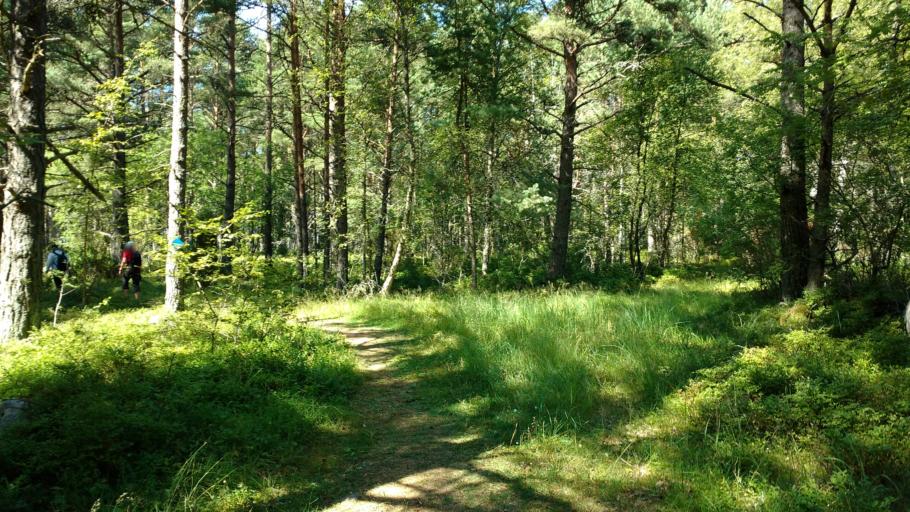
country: FI
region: Varsinais-Suomi
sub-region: Aboland-Turunmaa
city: Dragsfjaerd
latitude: 59.8096
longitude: 22.3192
